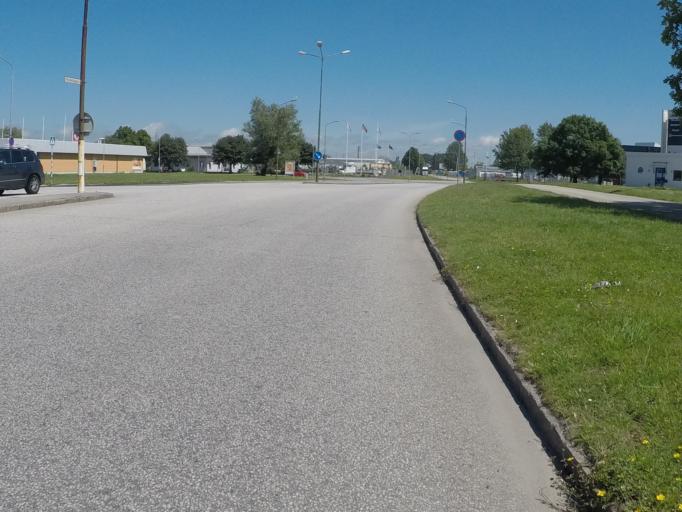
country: SE
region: Skane
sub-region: Burlovs Kommun
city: Arloev
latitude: 55.6449
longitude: 13.0814
